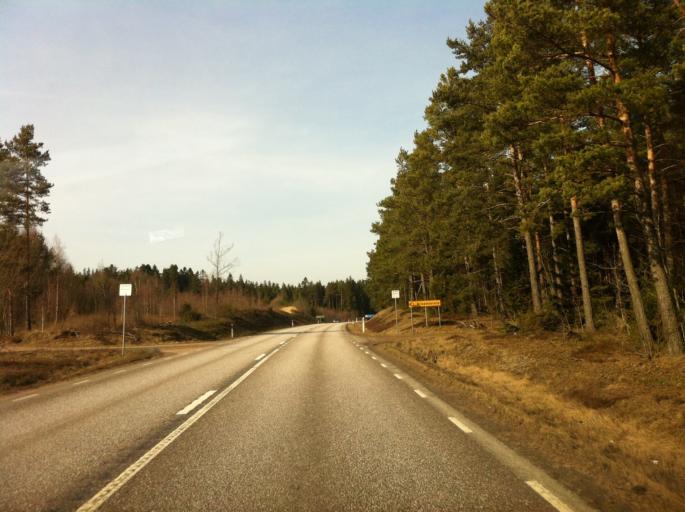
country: SE
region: Vaestra Goetaland
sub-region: Skovde Kommun
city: Skultorp
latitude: 58.2412
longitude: 13.8220
